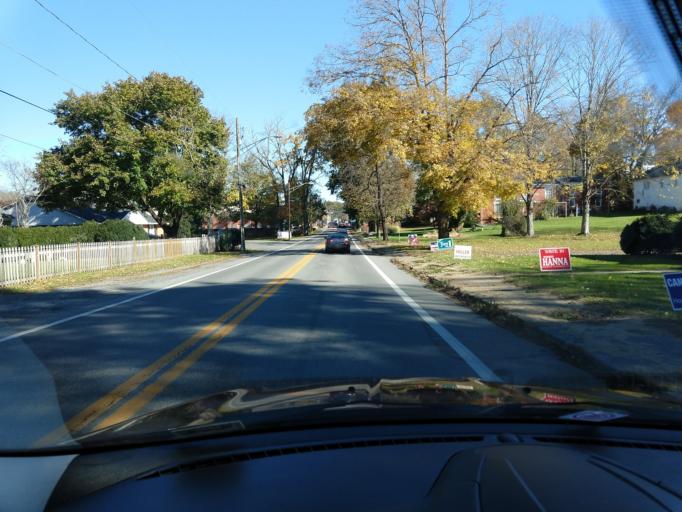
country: US
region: West Virginia
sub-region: Greenbrier County
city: Lewisburg
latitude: 37.7996
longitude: -80.4474
